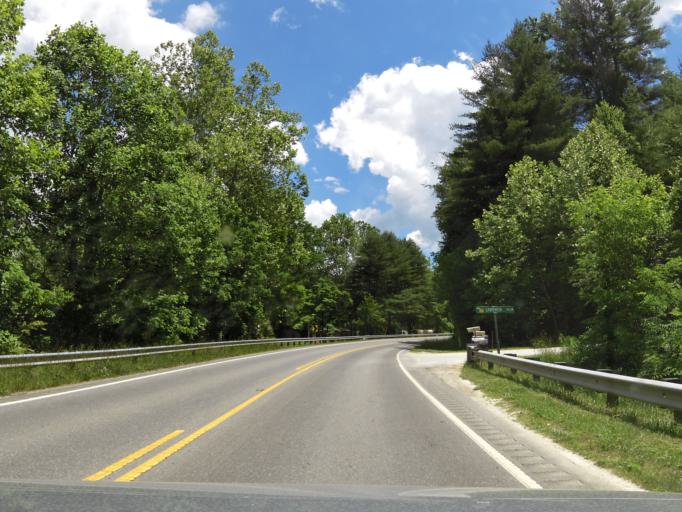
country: US
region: North Carolina
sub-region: Graham County
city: Robbinsville
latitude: 35.2876
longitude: -83.7682
